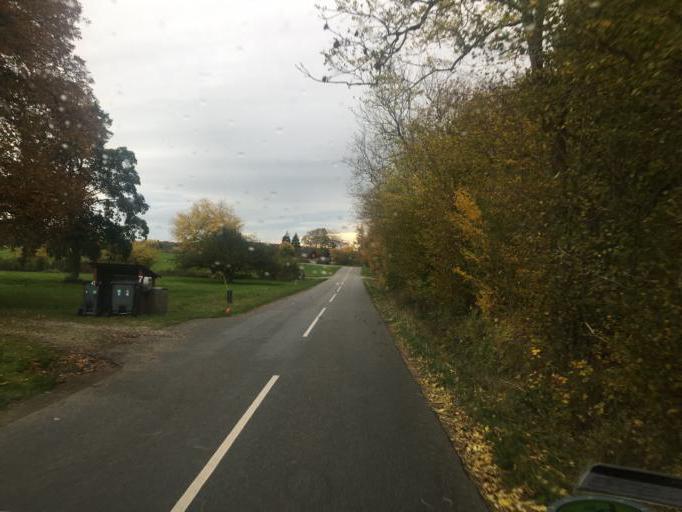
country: DK
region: Zealand
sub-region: Koge Kommune
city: Bjaeverskov
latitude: 55.4160
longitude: 11.9841
